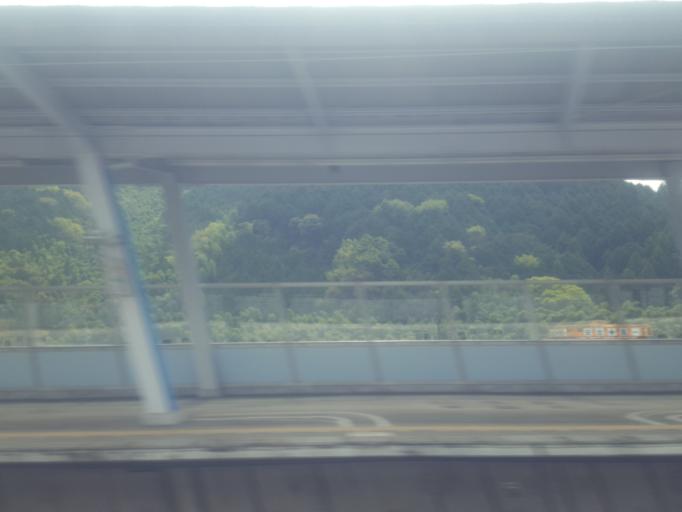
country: JP
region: Yamaguchi
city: Iwakuni
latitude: 34.1631
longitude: 132.1488
